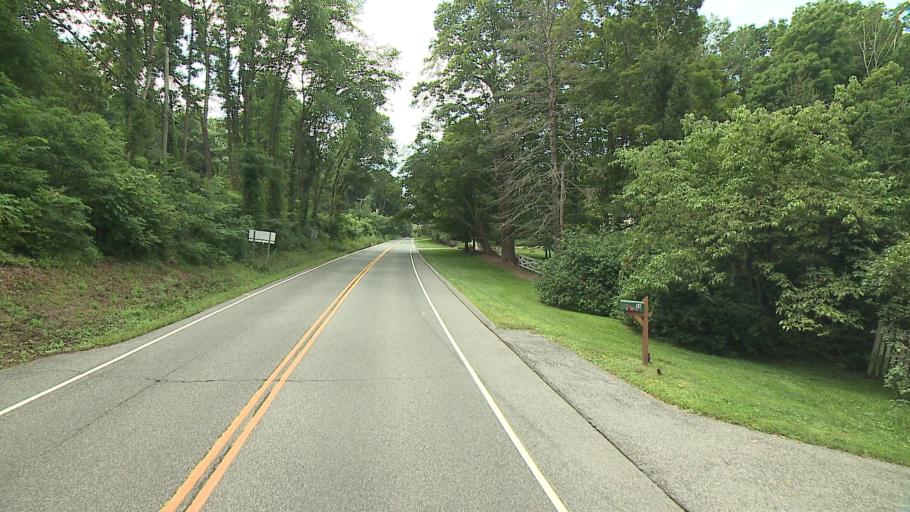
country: US
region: Connecticut
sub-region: Fairfield County
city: Sherman
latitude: 41.5945
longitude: -73.4975
